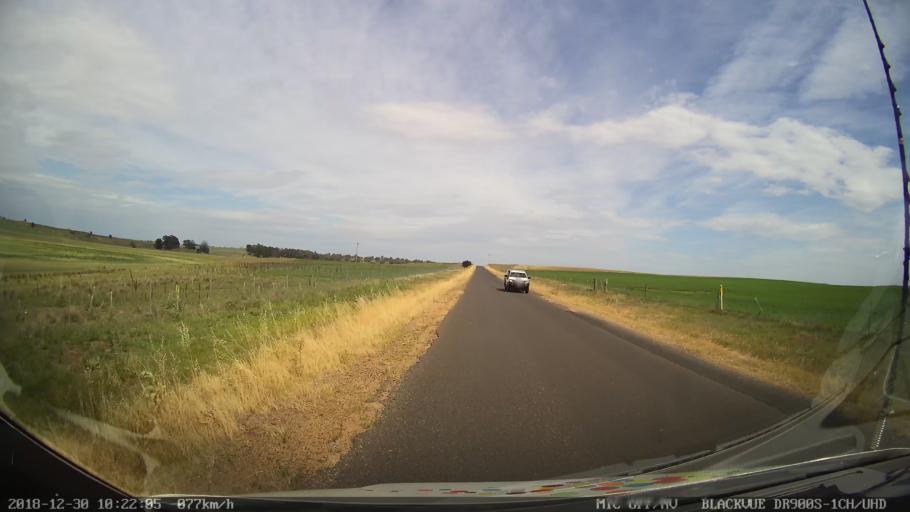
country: AU
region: New South Wales
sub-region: Snowy River
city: Berridale
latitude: -36.5465
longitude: 148.9996
